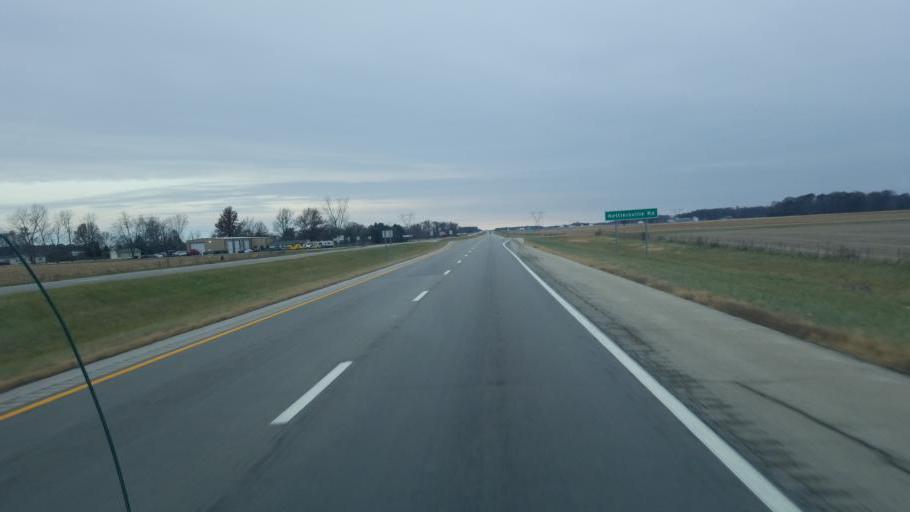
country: US
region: Ohio
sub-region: Auglaize County
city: Wapakoneta
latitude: 40.5648
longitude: -84.2574
